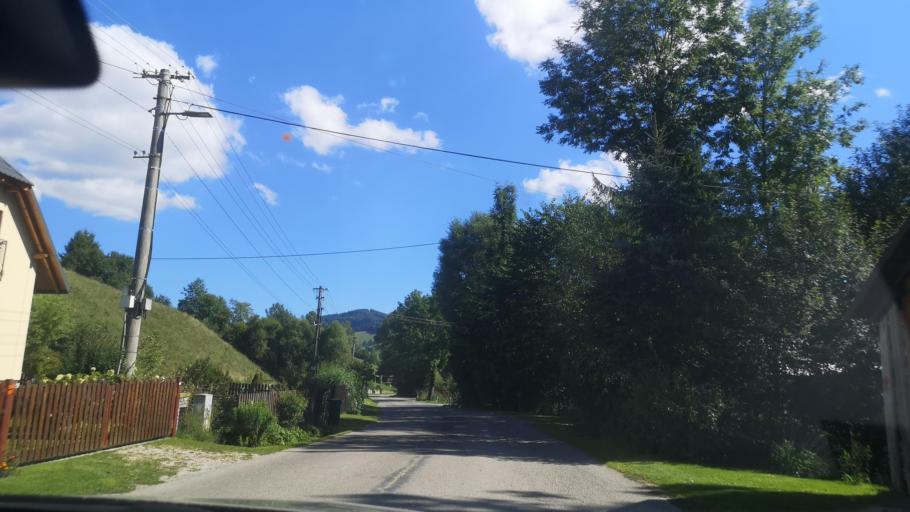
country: SK
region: Zilinsky
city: Oravska Lesna
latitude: 49.2747
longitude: 19.1382
